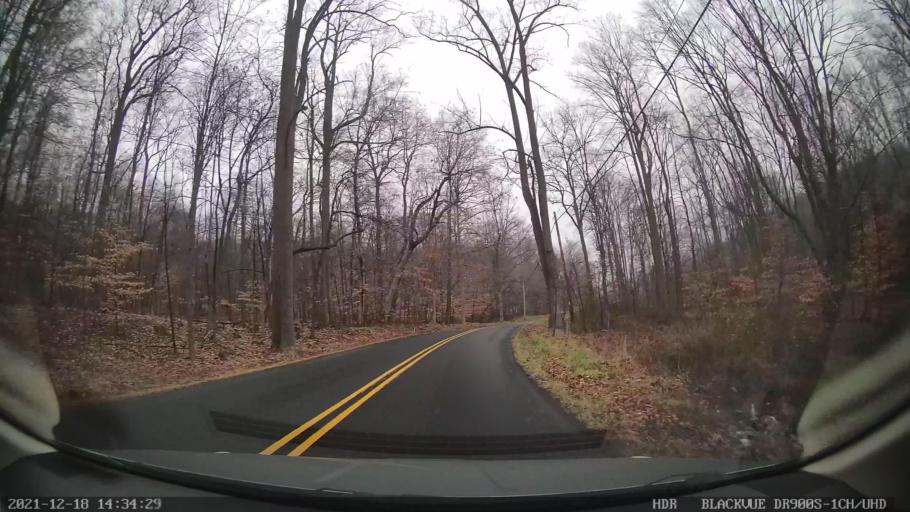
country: US
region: Pennsylvania
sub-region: Berks County
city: New Berlinville
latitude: 40.3852
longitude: -75.6712
